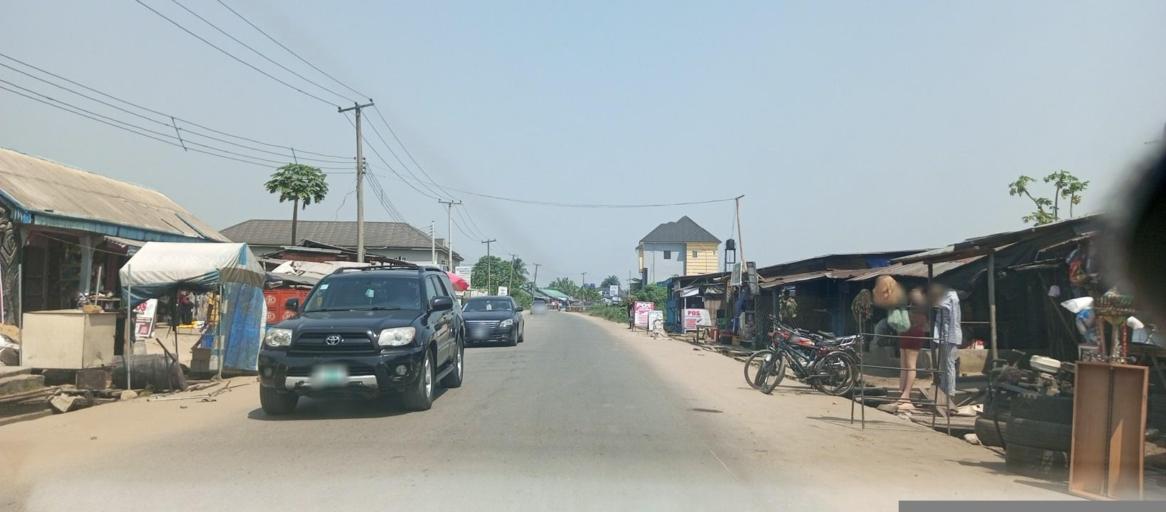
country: NG
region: Rivers
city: Emuoha
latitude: 4.9142
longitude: 6.9141
